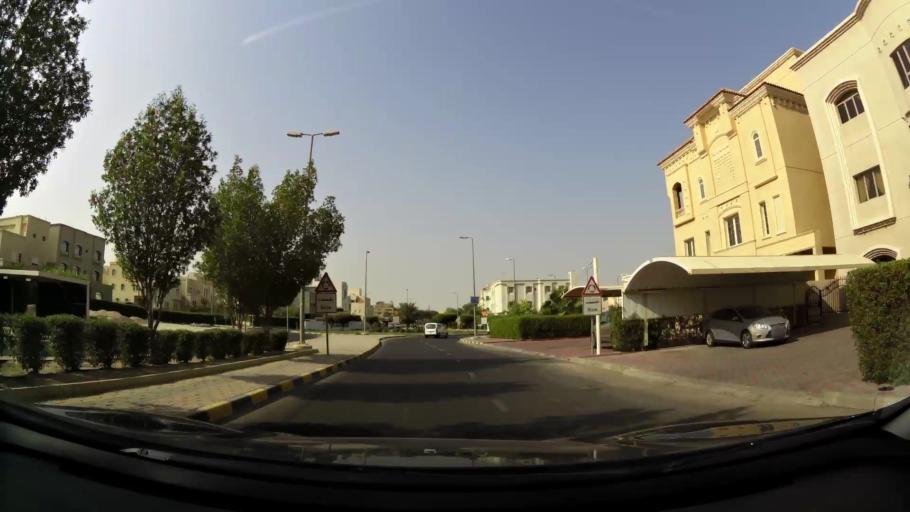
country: KW
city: Bayan
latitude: 29.2794
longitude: 48.0424
